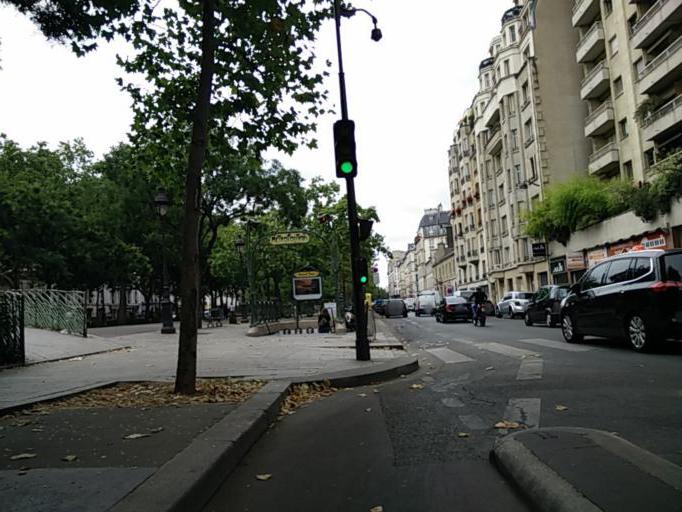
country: FR
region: Ile-de-France
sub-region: Paris
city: Paris
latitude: 48.8569
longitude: 2.3706
